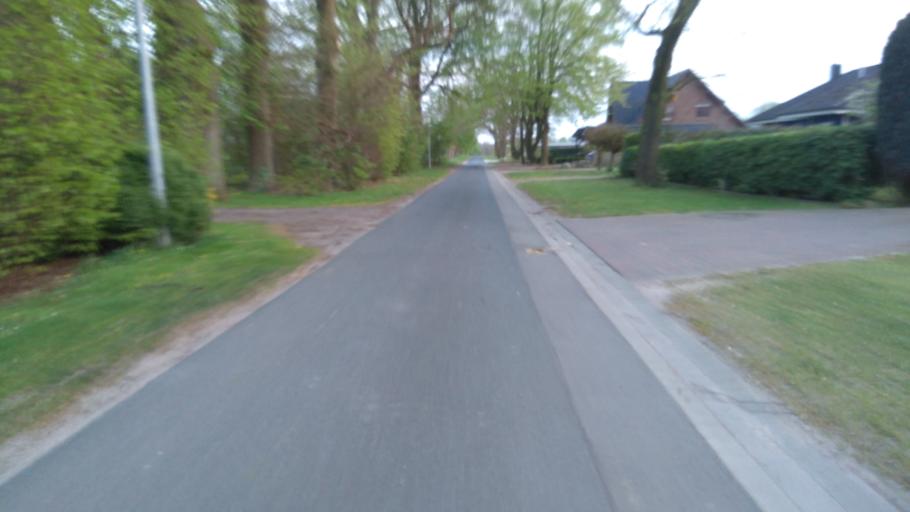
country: DE
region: Lower Saxony
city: Bargstedt
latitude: 53.4639
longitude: 9.4706
